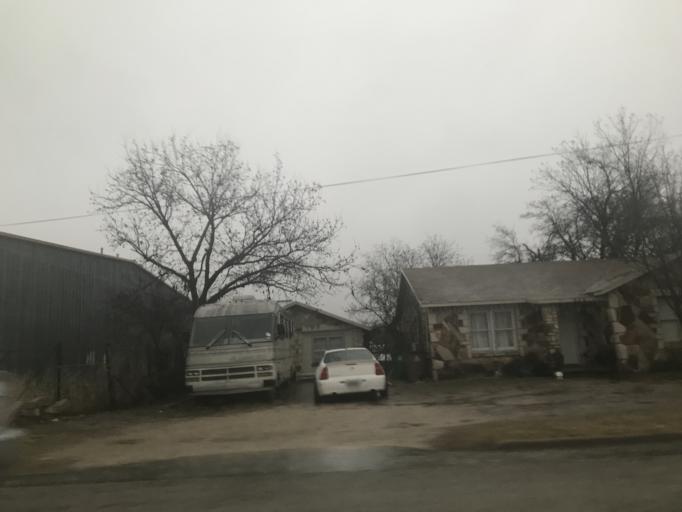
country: US
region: Texas
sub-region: Tom Green County
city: San Angelo
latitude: 31.4702
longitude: -100.4174
